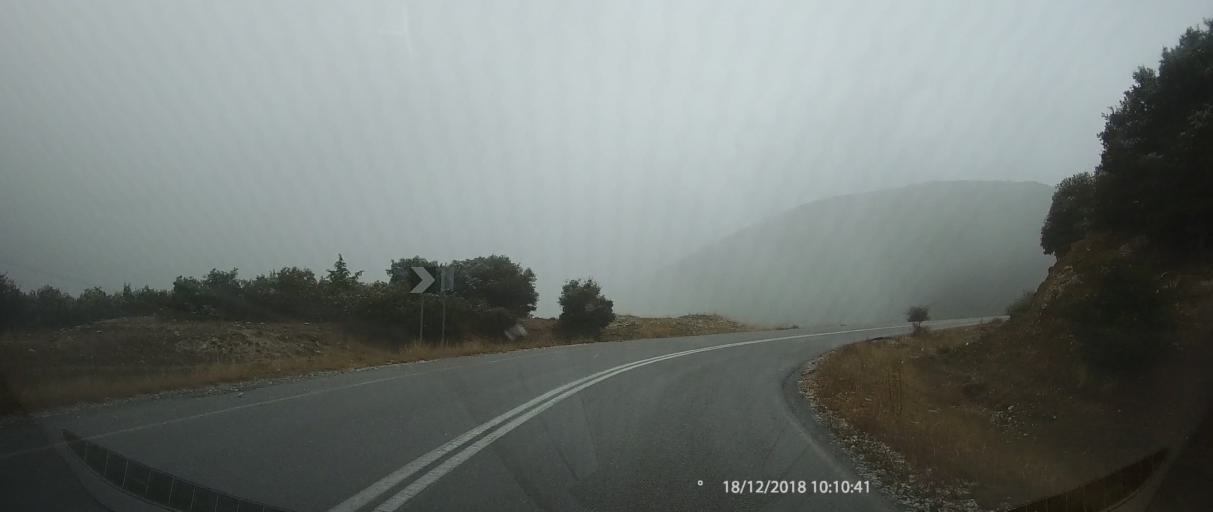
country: GR
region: Thessaly
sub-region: Nomos Larisis
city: Livadi
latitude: 40.0897
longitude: 22.2105
